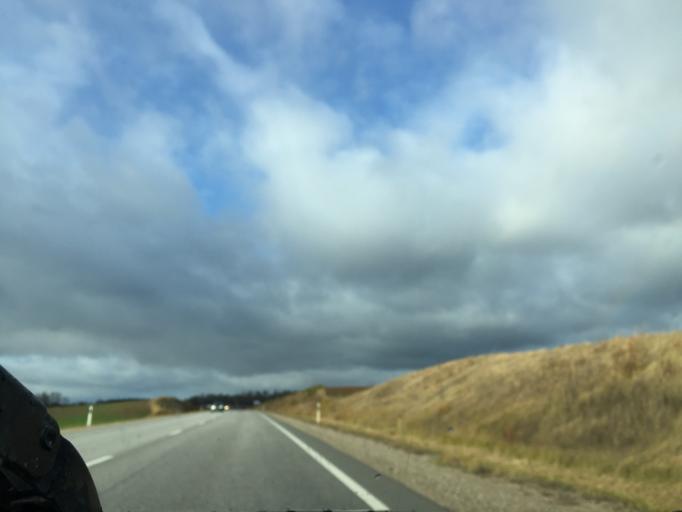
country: LV
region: Tukuma Rajons
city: Tukums
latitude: 56.9745
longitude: 23.0556
